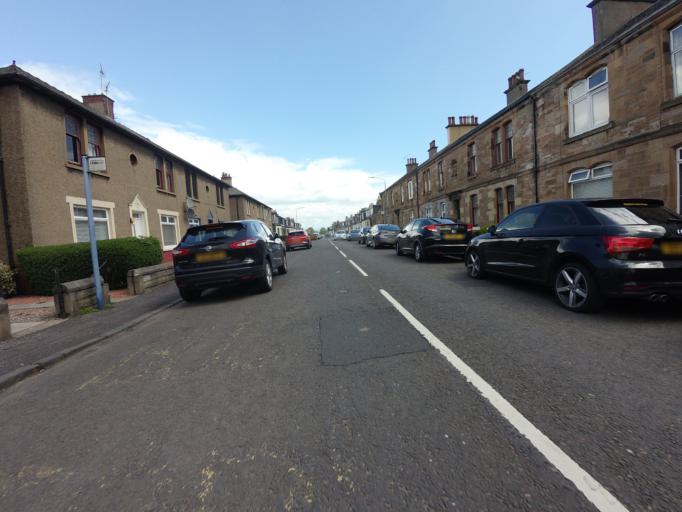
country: GB
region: Scotland
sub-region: Falkirk
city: Falkirk
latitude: 56.0123
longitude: -3.7921
